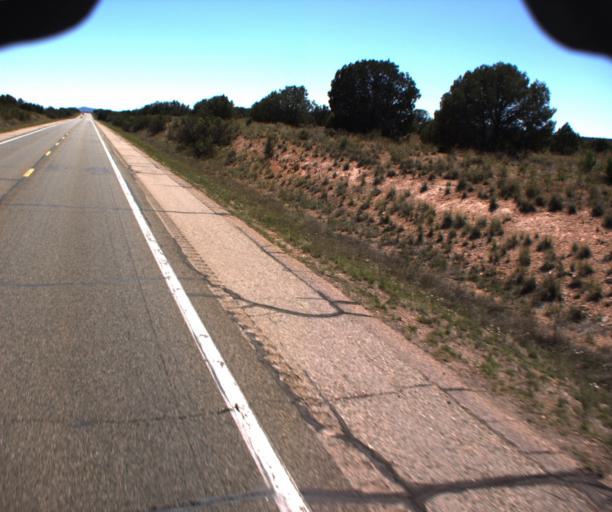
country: US
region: Arizona
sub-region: Yavapai County
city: Paulden
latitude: 34.9574
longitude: -112.4173
